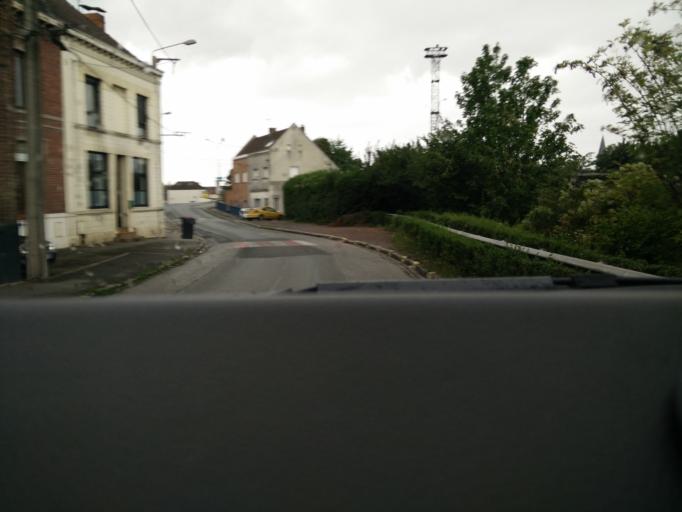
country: FR
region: Nord-Pas-de-Calais
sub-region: Departement du Pas-de-Calais
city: Grenay
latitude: 50.4457
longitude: 2.7398
